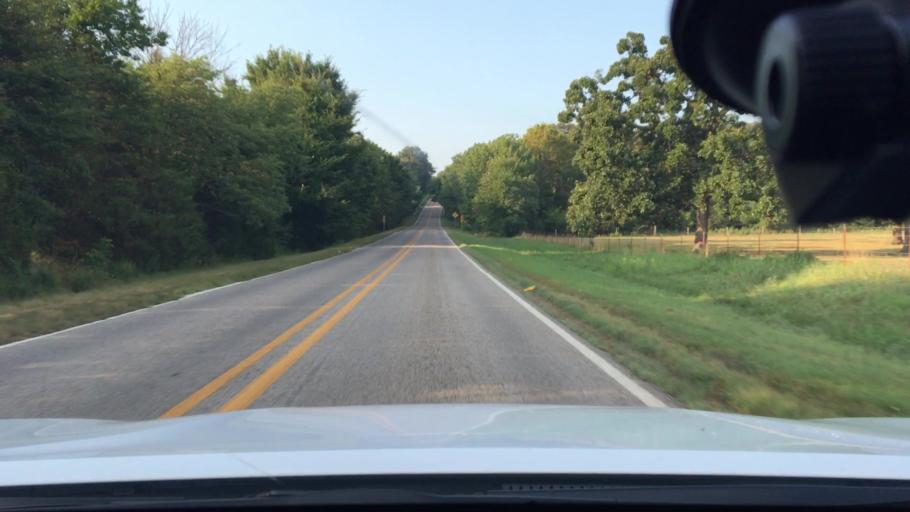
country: US
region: Arkansas
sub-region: Logan County
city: Paris
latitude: 35.3169
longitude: -93.6324
